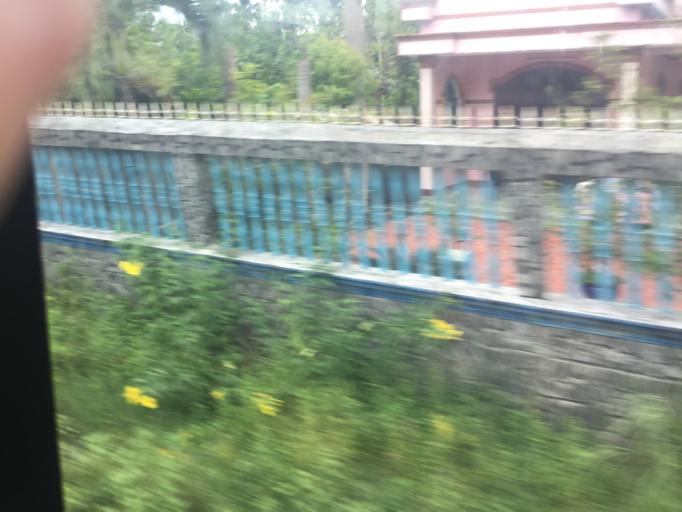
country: VN
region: Ho Chi Minh City
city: Cu Chi
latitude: 11.1211
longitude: 106.4788
